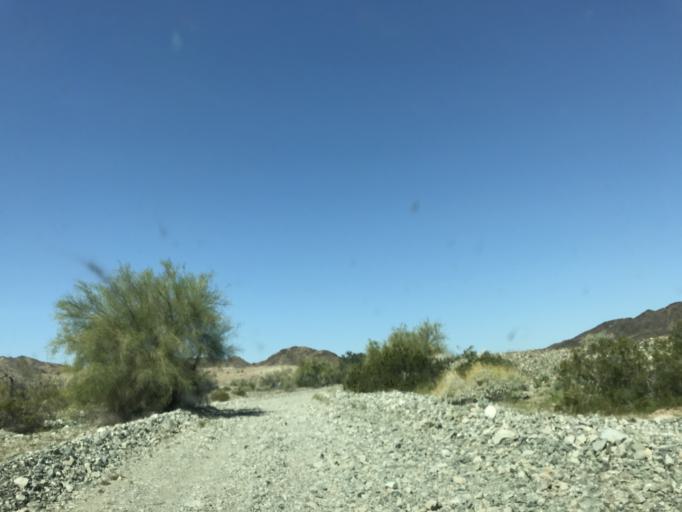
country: US
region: California
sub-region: Riverside County
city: Mesa Verde
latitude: 33.4933
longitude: -114.8259
